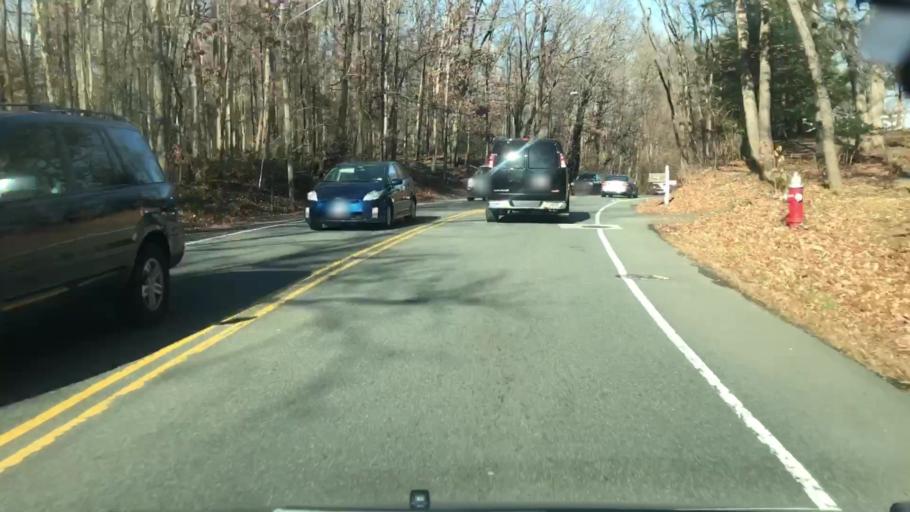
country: US
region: Virginia
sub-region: Fairfax County
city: Belle Haven
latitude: 38.7654
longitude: -77.0607
